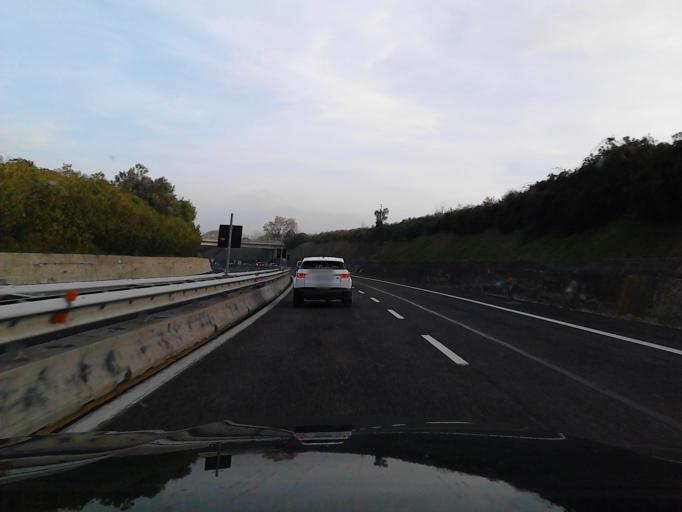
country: IT
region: Abruzzo
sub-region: Provincia di Chieti
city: Ortona
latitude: 42.3165
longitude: 14.4018
